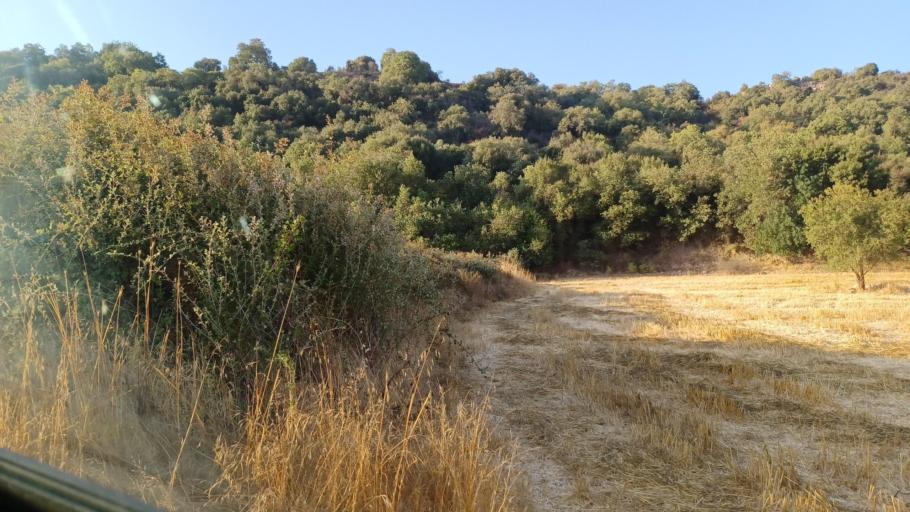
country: CY
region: Pafos
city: Tala
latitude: 34.9242
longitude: 32.4957
